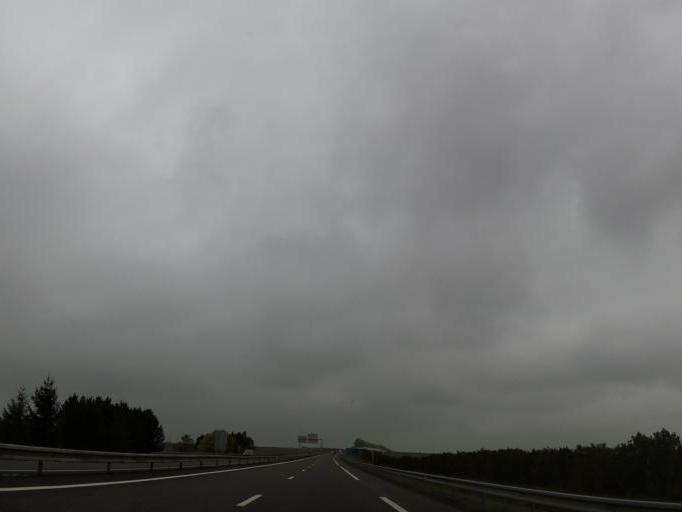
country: FR
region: Champagne-Ardenne
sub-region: Departement de la Marne
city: Courtisols
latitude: 49.0338
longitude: 4.4524
